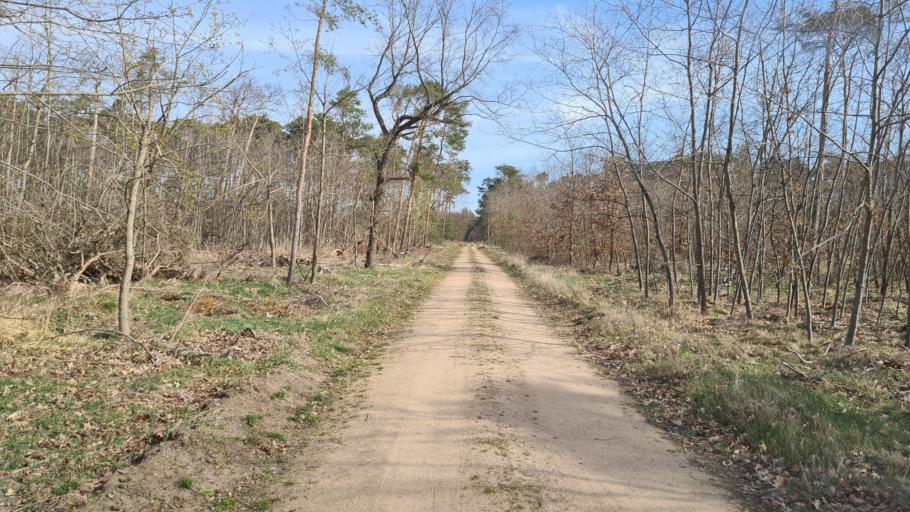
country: DE
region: Saxony
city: Nauwalde
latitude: 51.4608
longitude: 13.3955
